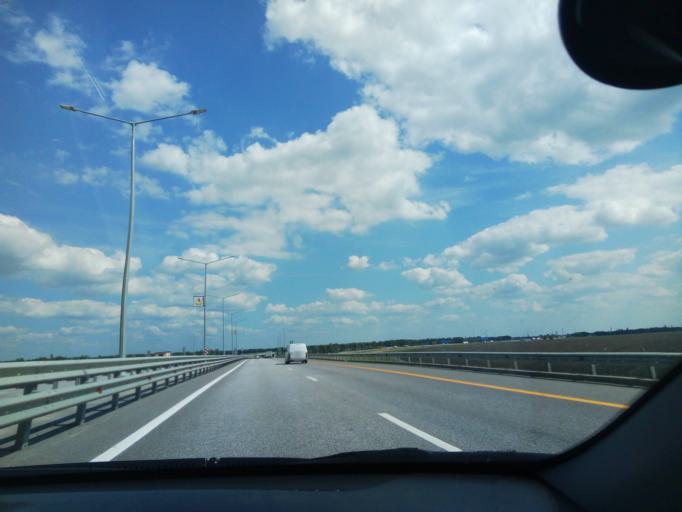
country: RU
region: Voronezj
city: Kashirskoye
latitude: 51.4818
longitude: 39.5451
